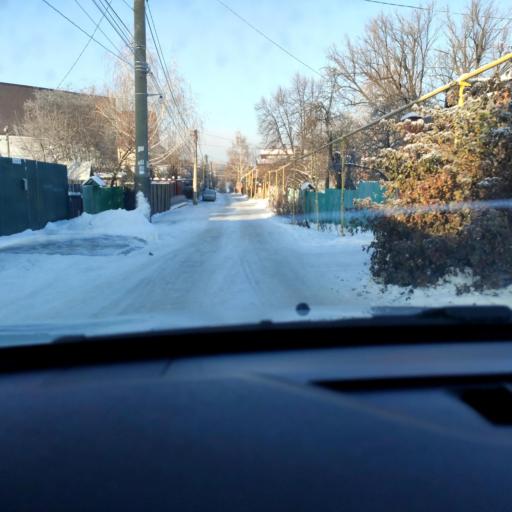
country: RU
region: Samara
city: Samara
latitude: 53.2712
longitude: 50.2043
